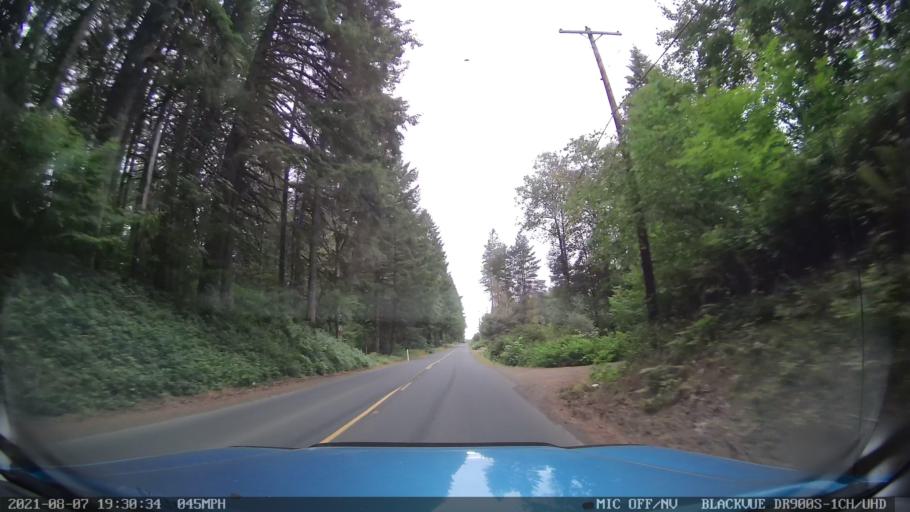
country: US
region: Oregon
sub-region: Linn County
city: Lyons
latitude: 44.8860
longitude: -122.6226
